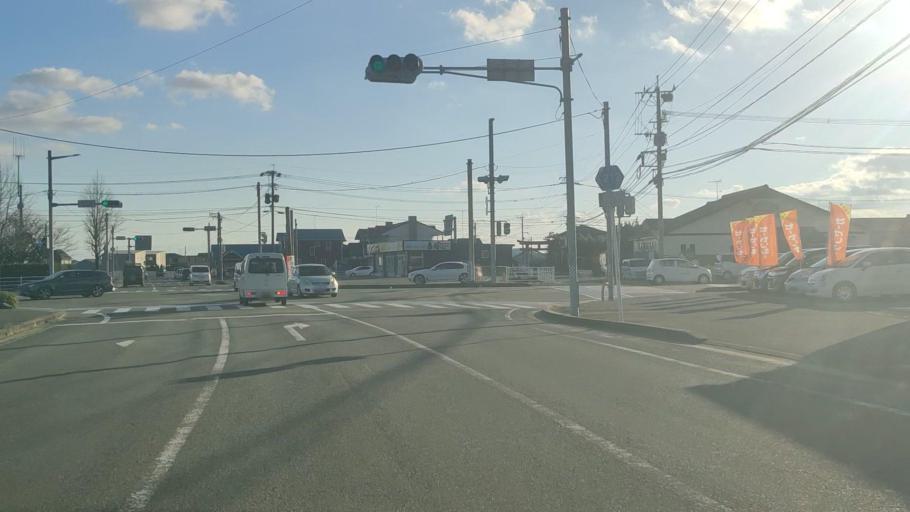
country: JP
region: Saga Prefecture
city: Saga-shi
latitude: 33.3094
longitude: 130.2644
